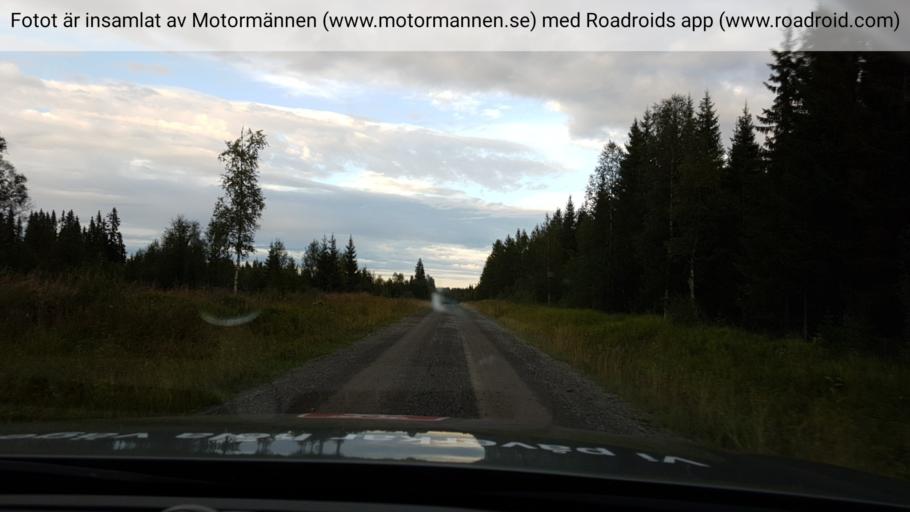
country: SE
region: Jaemtland
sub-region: OEstersunds Kommun
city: Lit
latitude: 63.4948
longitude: 15.2019
